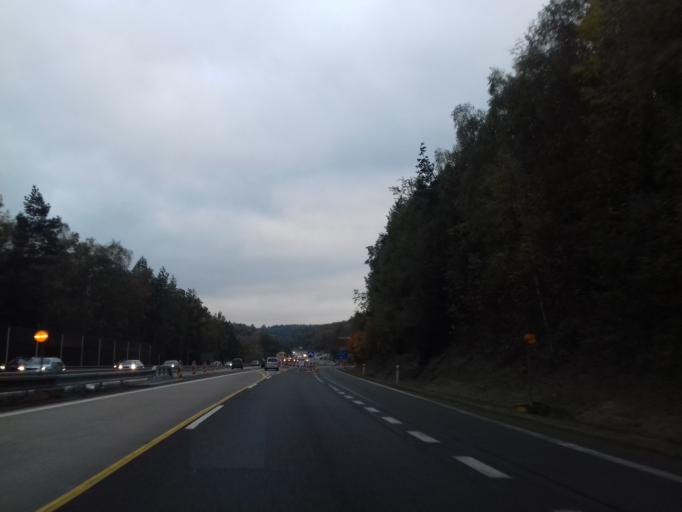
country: CZ
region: Central Bohemia
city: Ondrejov
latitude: 49.8671
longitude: 14.7825
